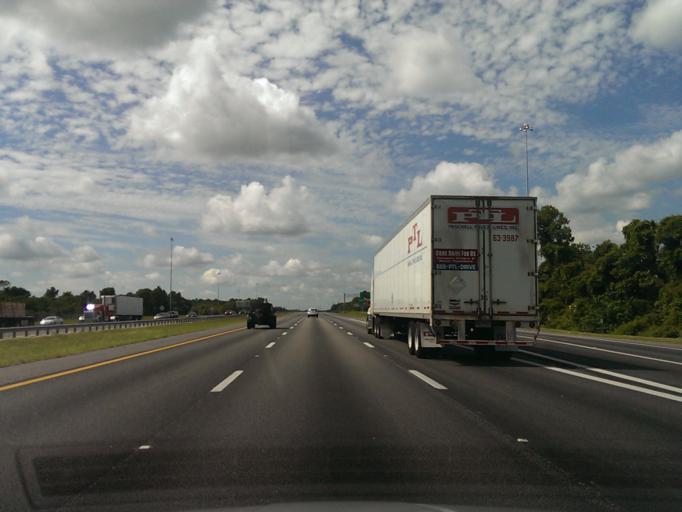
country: US
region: Florida
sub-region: Osceola County
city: Celebration
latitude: 28.3681
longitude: -81.5132
